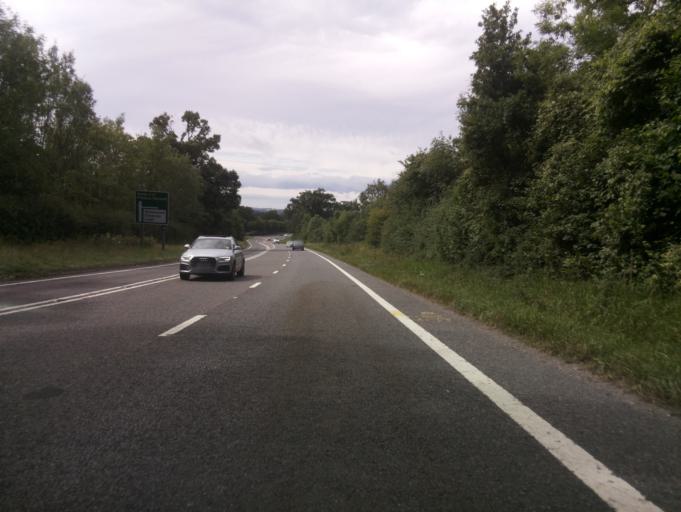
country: GB
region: England
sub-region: Somerset
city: Yeovil
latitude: 50.8582
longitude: -2.5894
